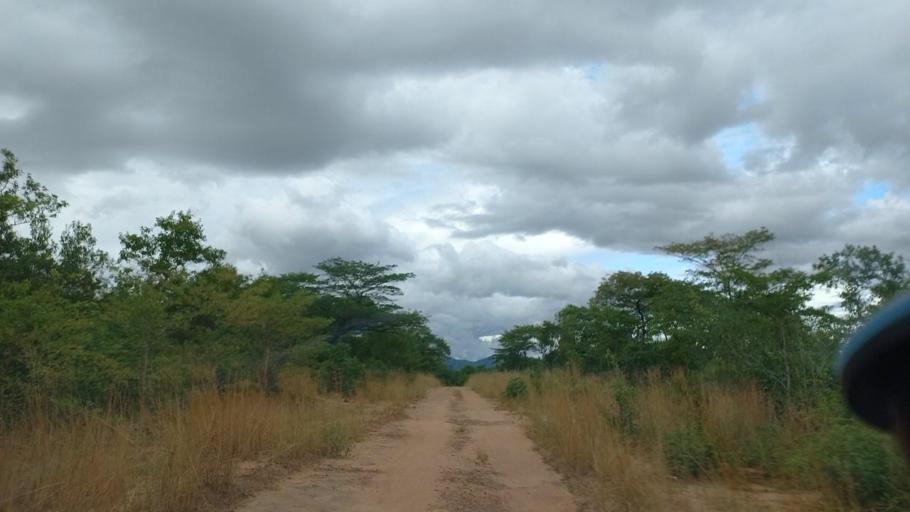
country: ZM
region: Lusaka
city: Luangwa
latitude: -15.5634
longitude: 30.3267
